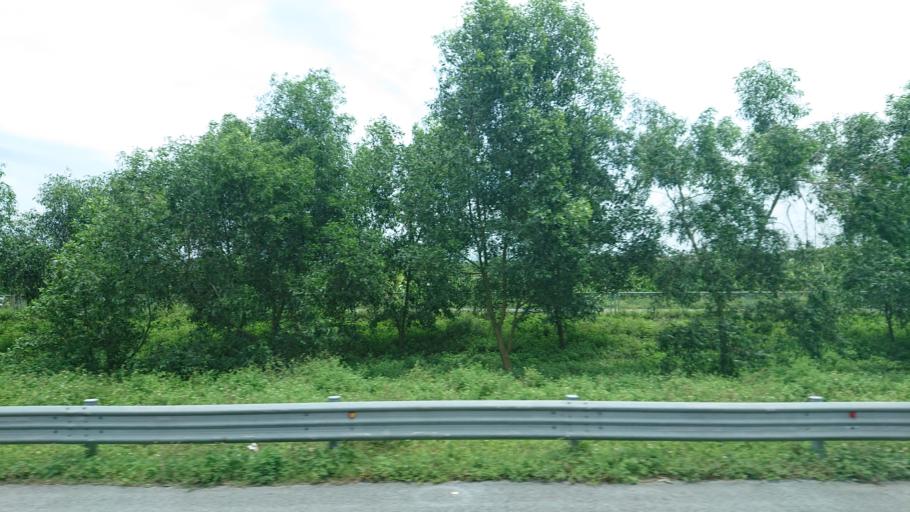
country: VN
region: Hai Phong
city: Nui Doi
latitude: 20.7658
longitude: 106.6563
